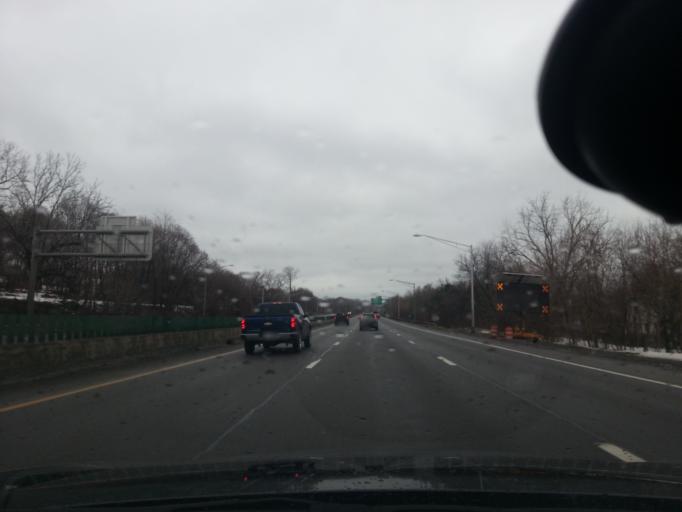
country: US
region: New York
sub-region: Onondaga County
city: Syracuse
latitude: 43.0325
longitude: -76.1425
